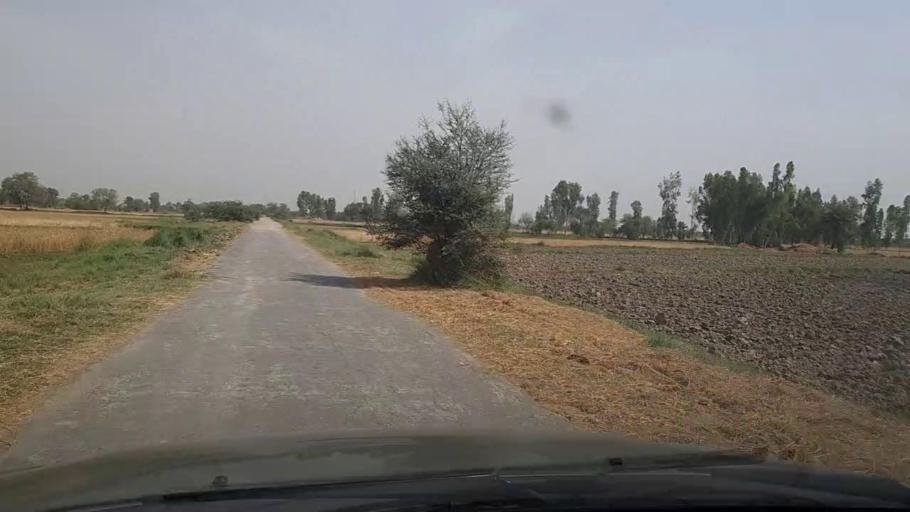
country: PK
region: Sindh
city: Lakhi
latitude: 27.8375
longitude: 68.7667
